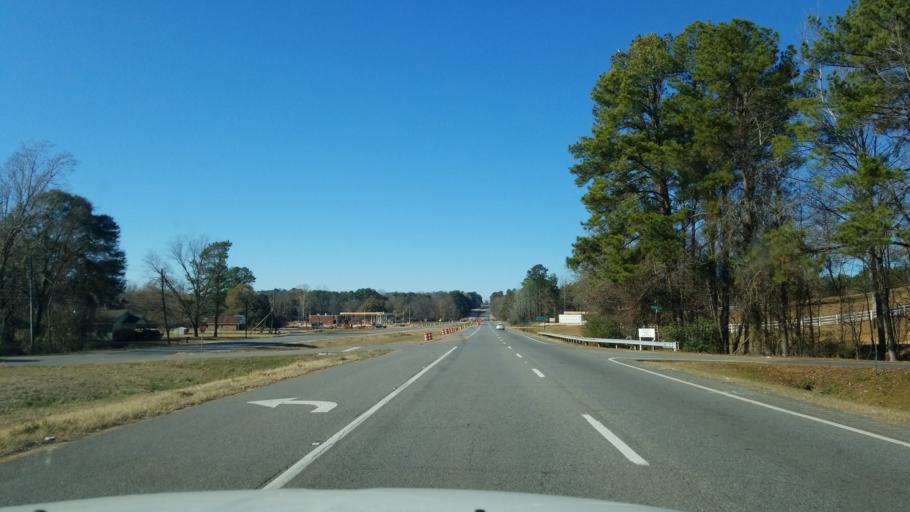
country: US
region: Alabama
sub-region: Tuscaloosa County
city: Northport
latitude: 33.2445
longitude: -87.6703
